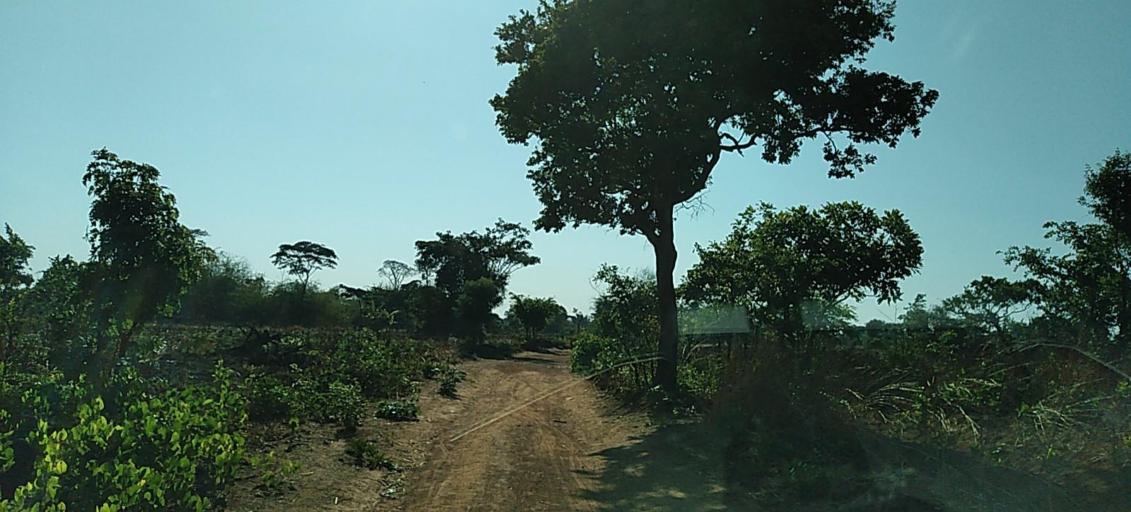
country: ZM
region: Copperbelt
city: Chililabombwe
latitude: -12.3691
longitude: 27.9109
